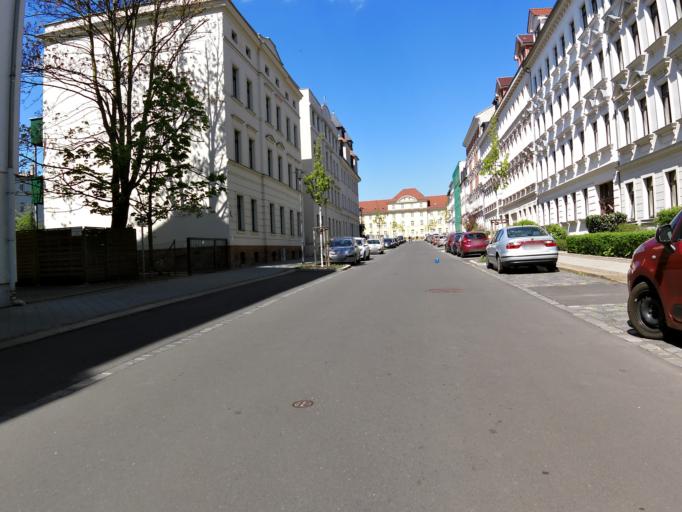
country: DE
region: Saxony
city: Leipzig
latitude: 51.3643
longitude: 12.3506
